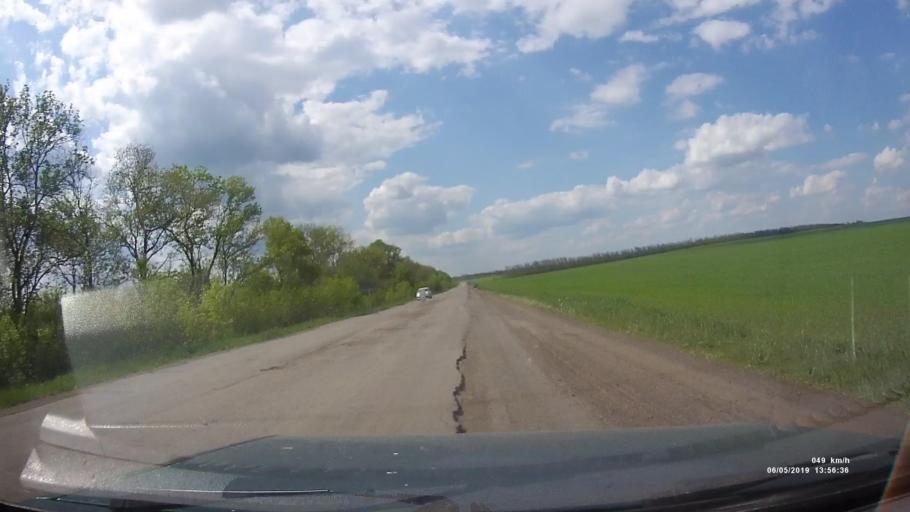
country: RU
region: Rostov
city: Melikhovskaya
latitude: 47.6816
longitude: 40.4296
